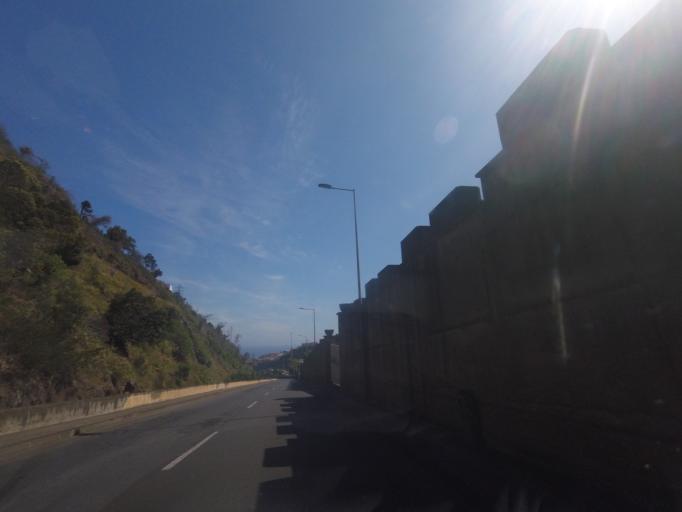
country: PT
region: Madeira
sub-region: Funchal
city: Nossa Senhora do Monte
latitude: 32.6682
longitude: -16.9191
